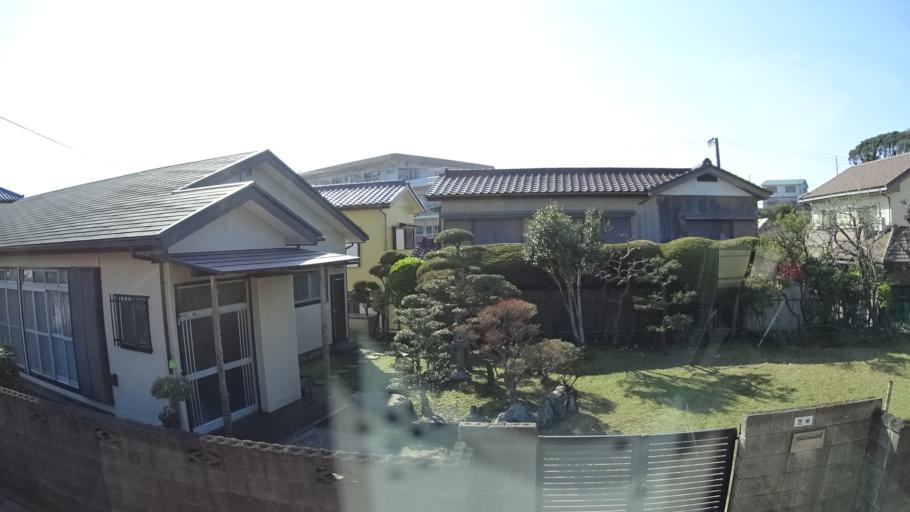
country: JP
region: Kanagawa
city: Miura
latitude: 35.1604
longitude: 139.6411
